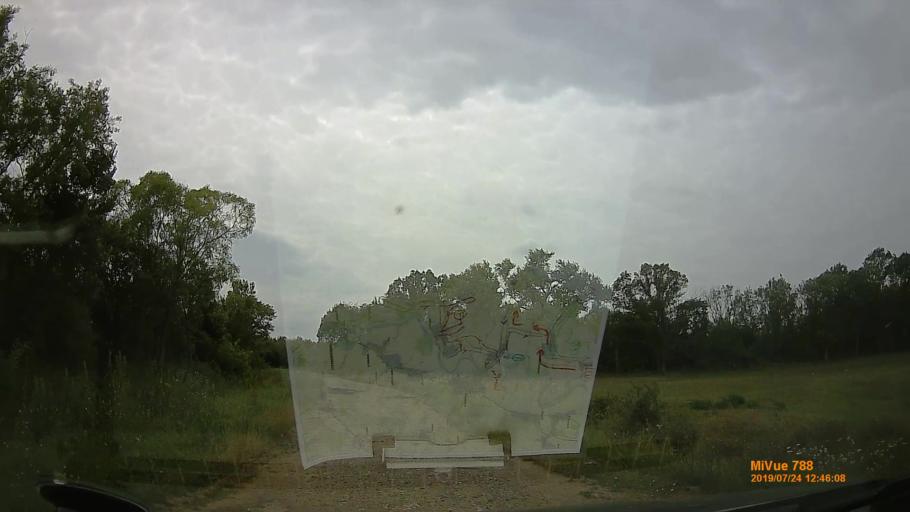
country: HU
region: Szabolcs-Szatmar-Bereg
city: Aranyosapati
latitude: 48.1975
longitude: 22.3208
